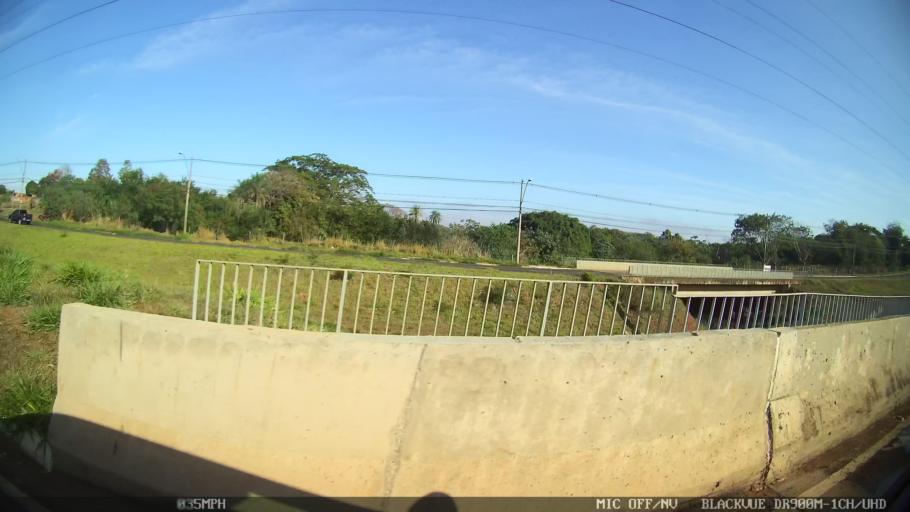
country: BR
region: Sao Paulo
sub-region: Sao Jose Do Rio Preto
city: Sao Jose do Rio Preto
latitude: -20.7846
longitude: -49.3433
